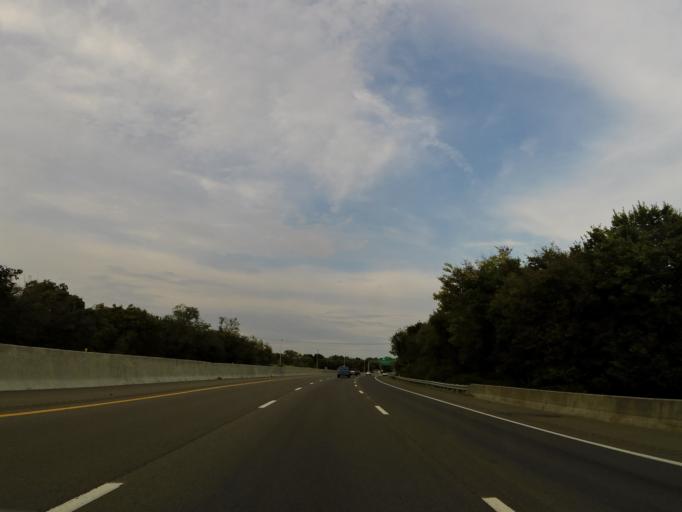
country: US
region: Tennessee
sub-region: Davidson County
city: Belle Meade
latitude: 36.1491
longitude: -86.8749
